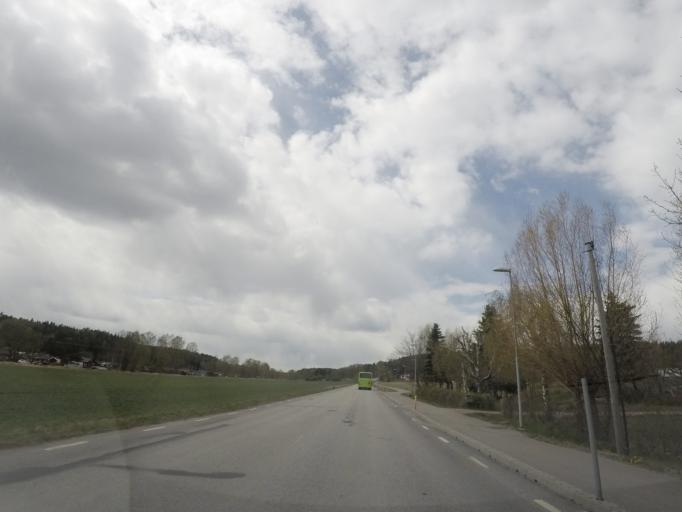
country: SE
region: Soedermanland
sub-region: Nykopings Kommun
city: Nykoping
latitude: 58.7409
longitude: 16.9379
